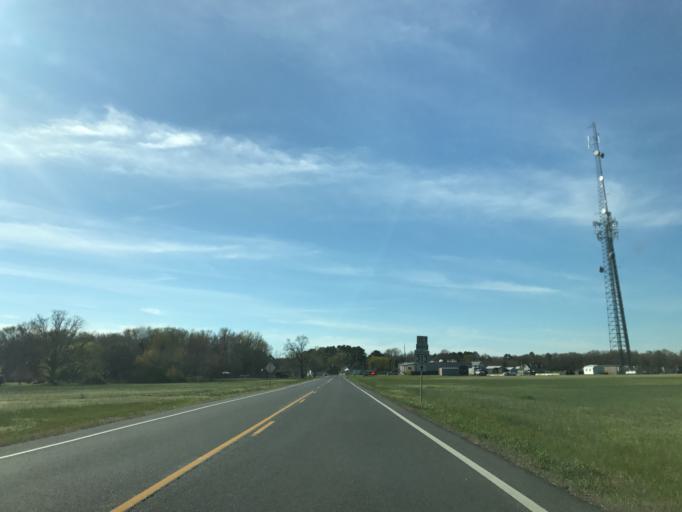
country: US
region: Maryland
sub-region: Caroline County
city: Greensboro
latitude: 39.0381
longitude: -75.7863
